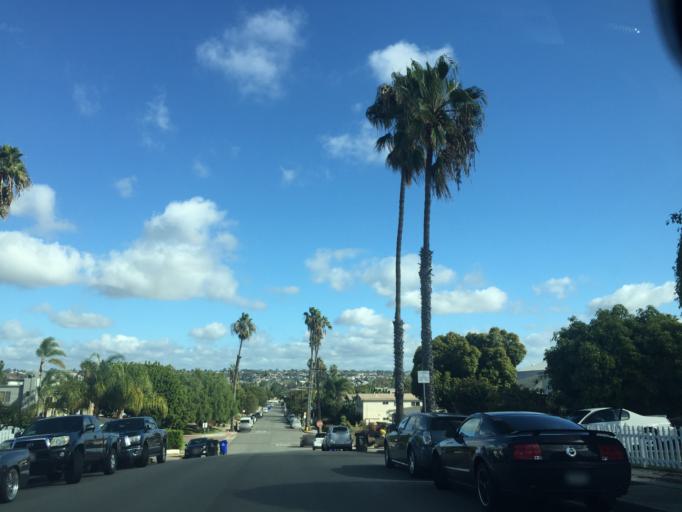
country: US
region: California
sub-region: San Diego County
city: La Jolla
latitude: 32.7964
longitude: -117.2331
